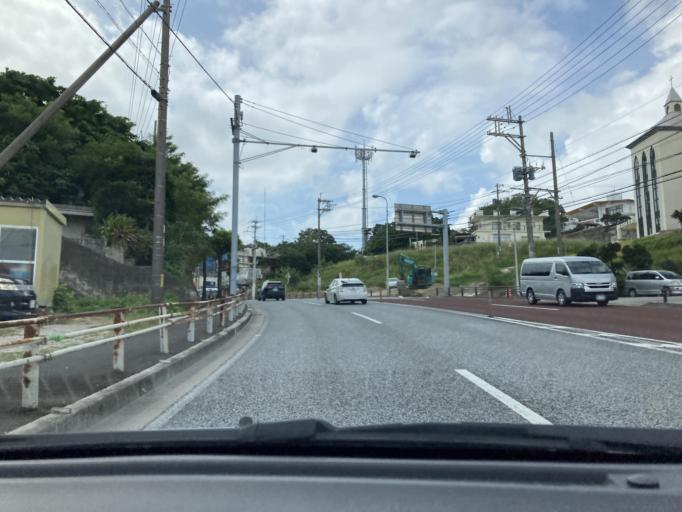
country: JP
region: Okinawa
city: Okinawa
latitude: 26.3176
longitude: 127.8194
